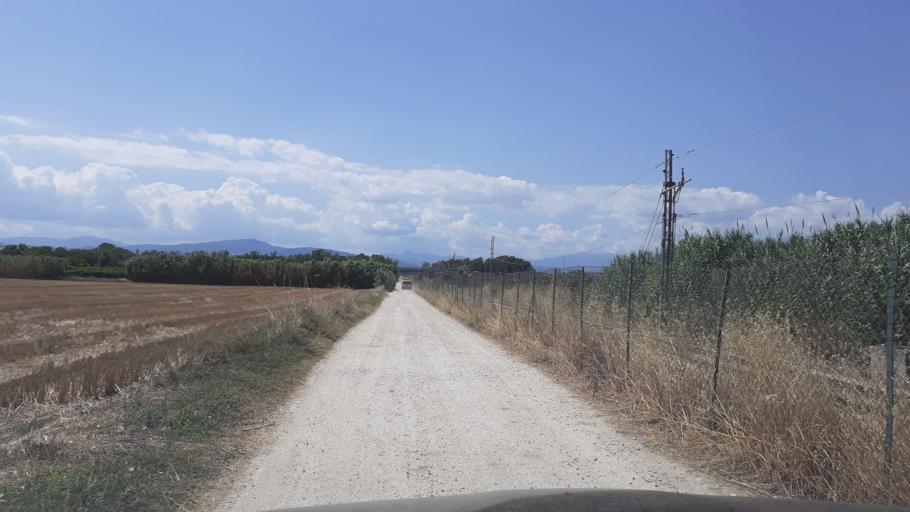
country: IT
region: Abruzzo
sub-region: Provincia di Chieti
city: Fossacesia
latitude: 42.2117
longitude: 14.4980
